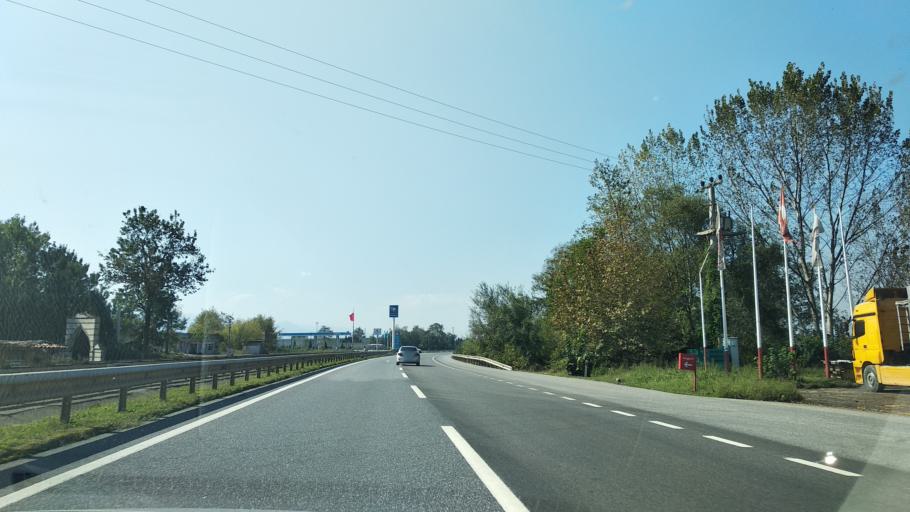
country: TR
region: Kocaeli
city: Derbent
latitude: 40.7300
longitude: 30.1500
